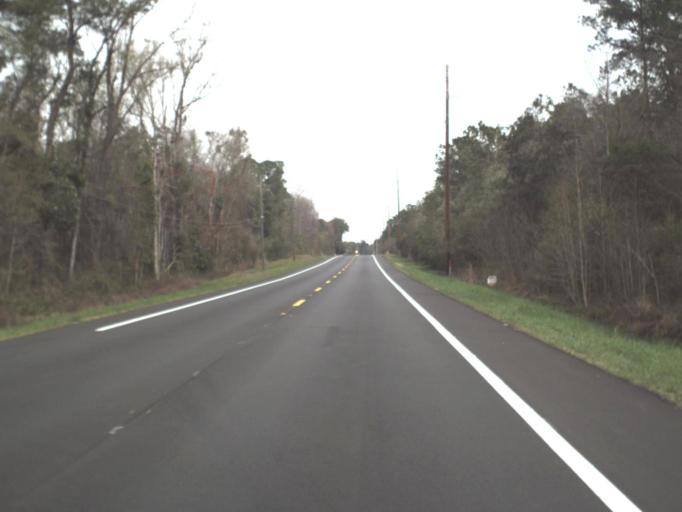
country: US
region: Florida
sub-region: Gadsden County
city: Midway
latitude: 30.3980
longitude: -84.6023
